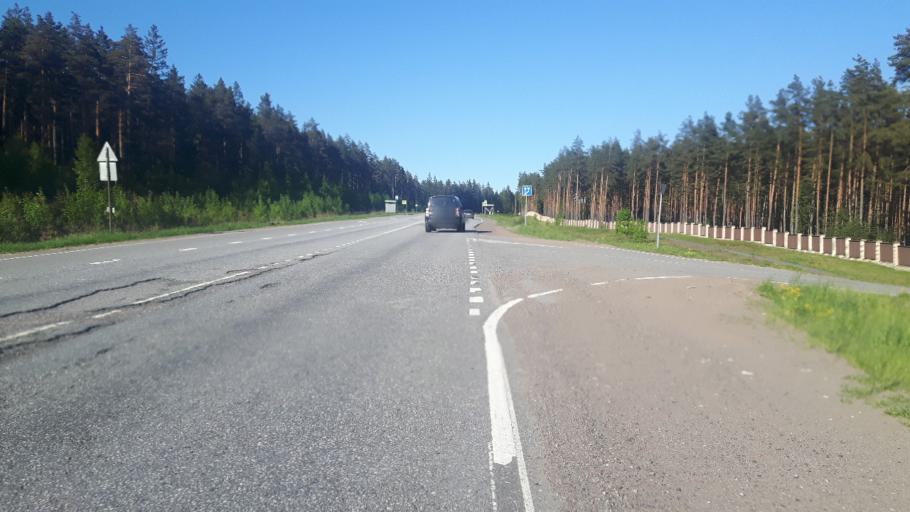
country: RU
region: Leningrad
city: Molodezhnoye
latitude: 60.1710
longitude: 29.2813
